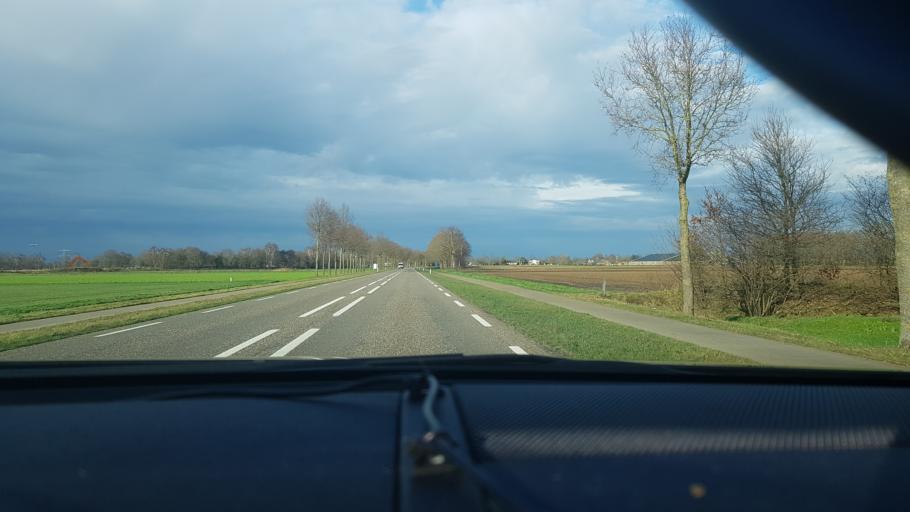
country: NL
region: Limburg
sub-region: Gemeente Venray
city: Venray
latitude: 51.4198
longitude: 5.9561
